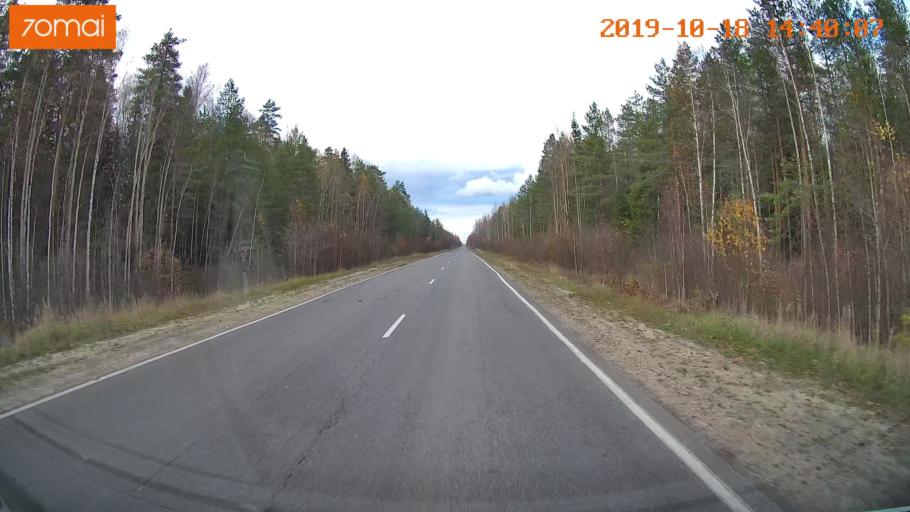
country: RU
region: Vladimir
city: Velikodvorskiy
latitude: 55.2717
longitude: 40.6684
